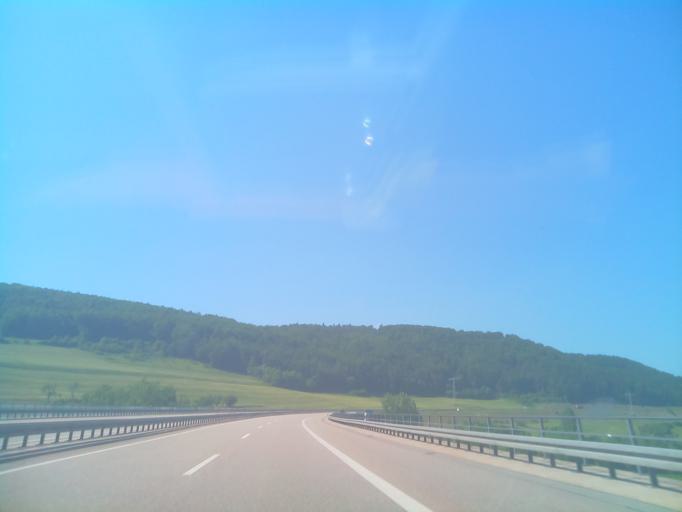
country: DE
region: Thuringia
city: Ellingshausen
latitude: 50.5510
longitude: 10.4764
